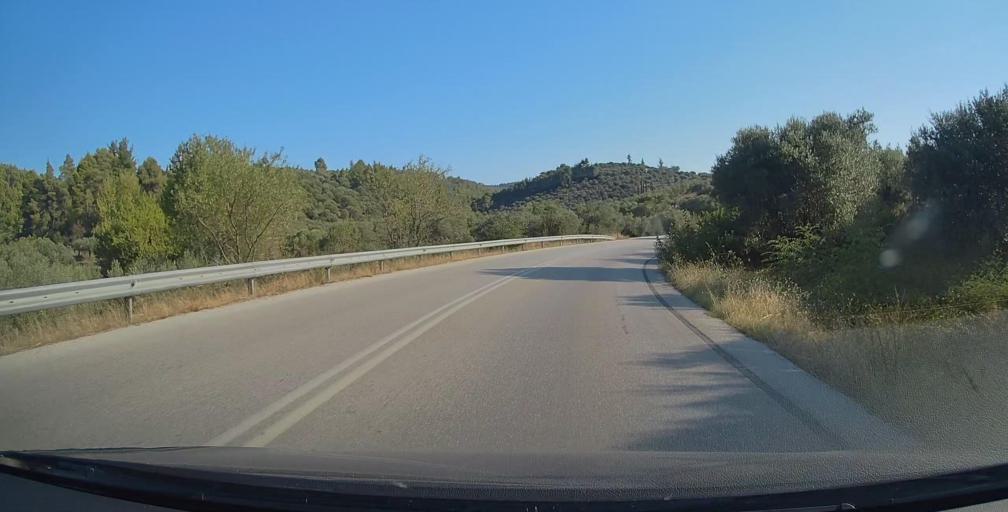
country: GR
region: Central Macedonia
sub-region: Nomos Chalkidikis
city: Neos Marmaras
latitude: 40.0843
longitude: 23.8090
